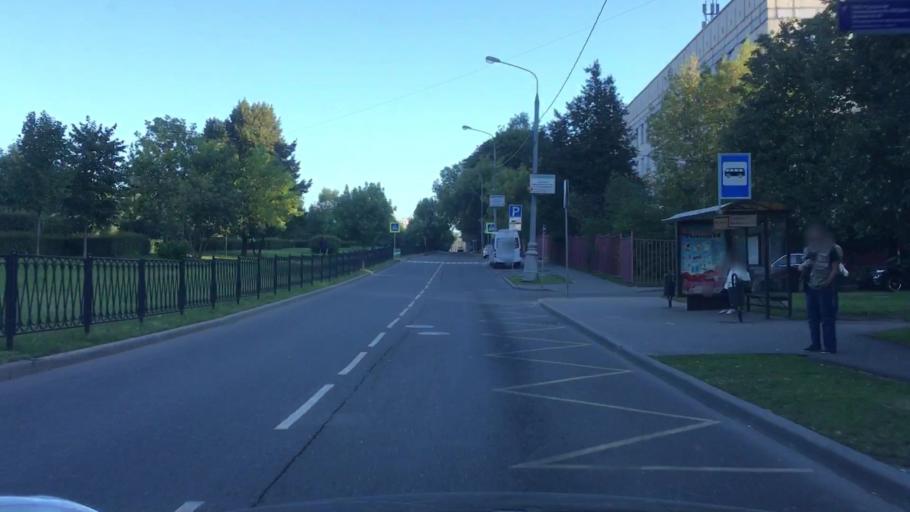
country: RU
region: Moscow
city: Davydkovo
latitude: 55.7209
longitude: 37.4622
